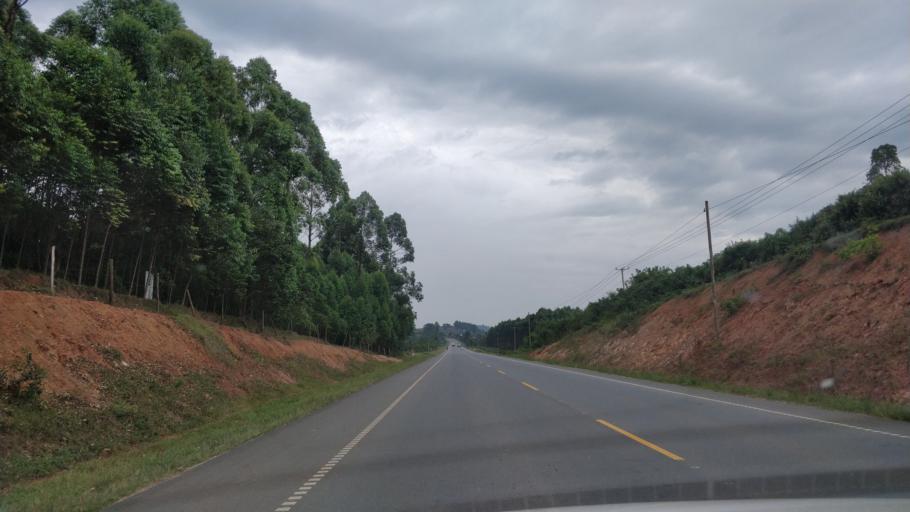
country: UG
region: Western Region
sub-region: Sheema District
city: Kibingo
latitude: -0.6575
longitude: 30.4716
